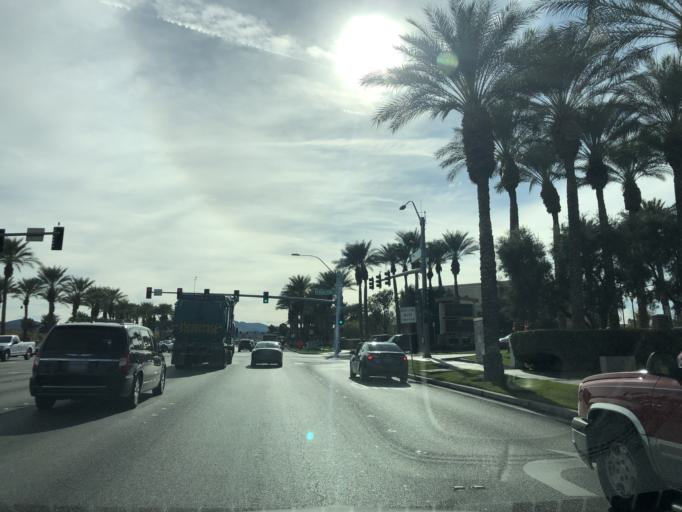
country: US
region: Nevada
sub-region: Clark County
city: Whitney
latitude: 36.0228
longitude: -115.0844
